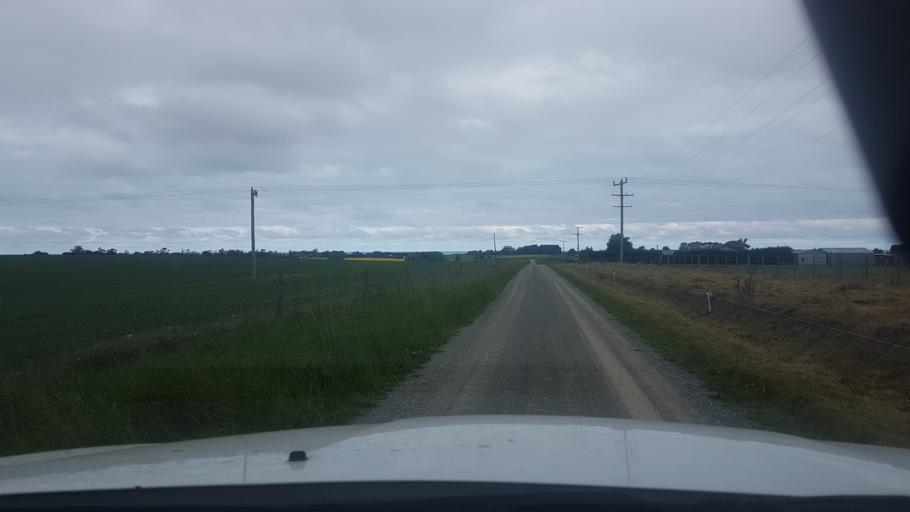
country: NZ
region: Canterbury
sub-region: Timaru District
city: Timaru
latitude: -44.4417
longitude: 171.1983
